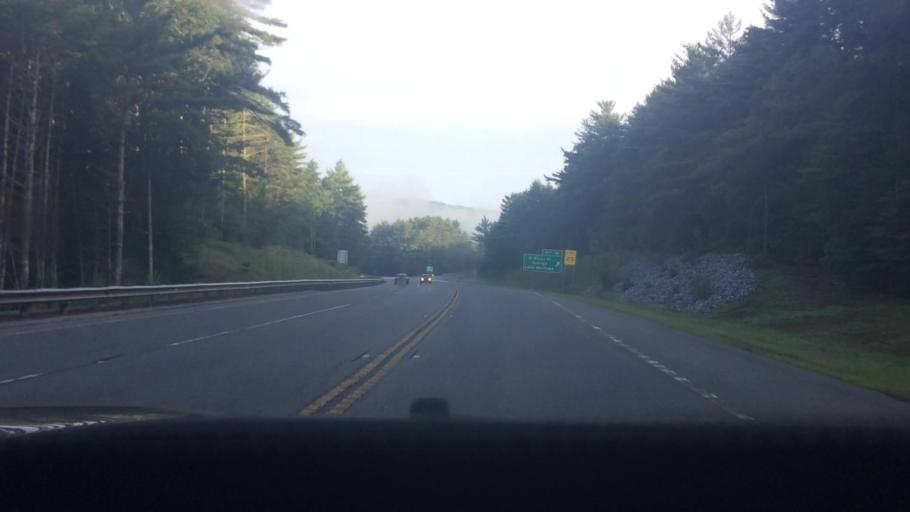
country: US
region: Massachusetts
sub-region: Franklin County
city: Orange
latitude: 42.5865
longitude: -72.3271
